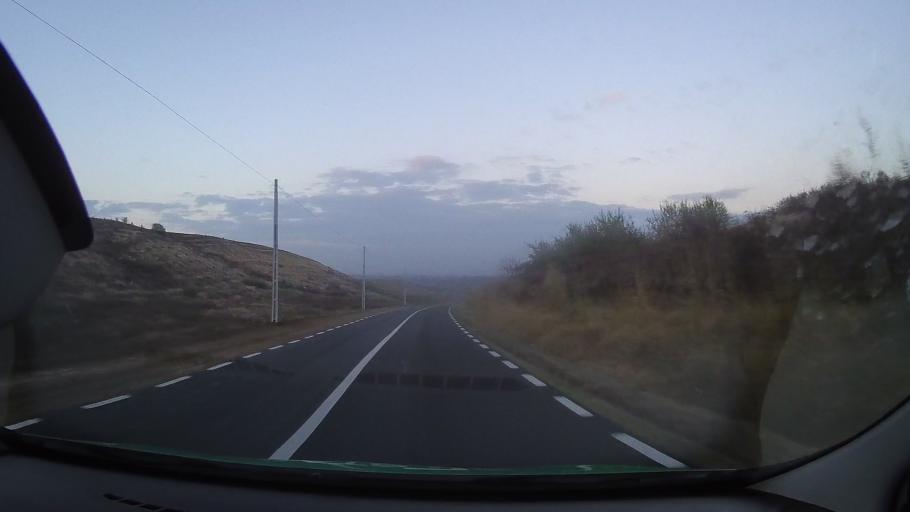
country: RO
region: Constanta
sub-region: Comuna Oltina
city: Oltina
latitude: 44.1392
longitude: 27.6653
